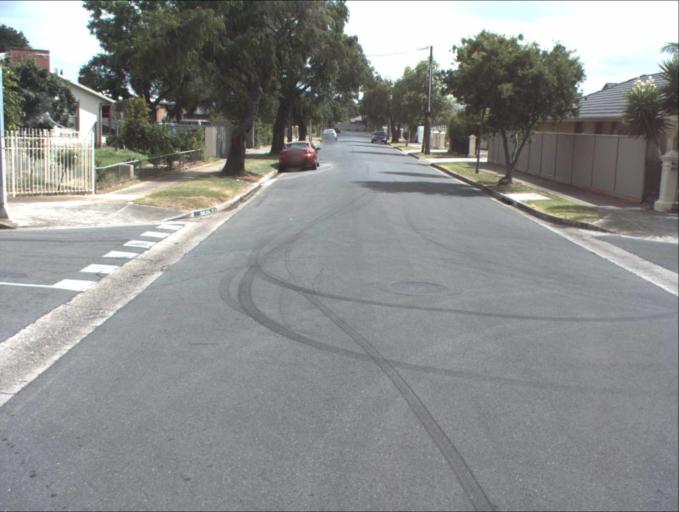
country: AU
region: South Australia
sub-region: Charles Sturt
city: Woodville
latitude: -34.8740
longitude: 138.5595
